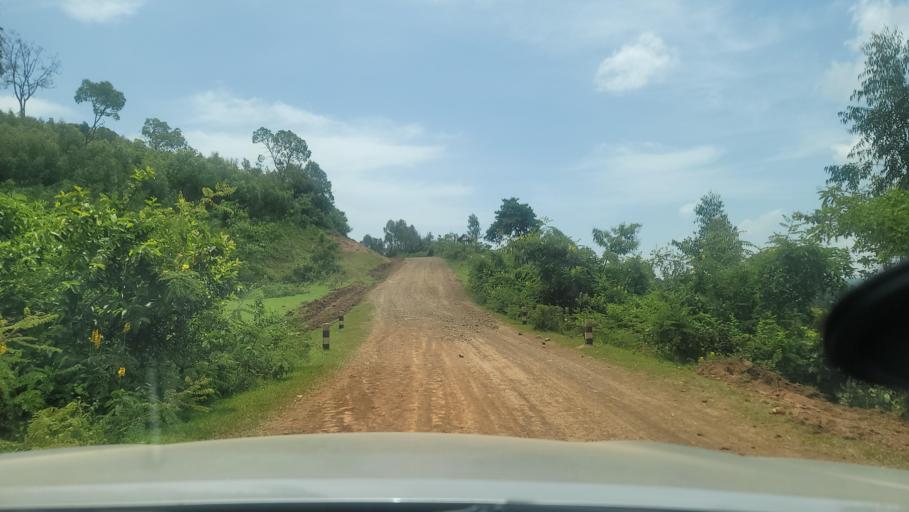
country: ET
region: Southern Nations, Nationalities, and People's Region
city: Bonga
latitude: 7.6966
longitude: 36.2458
